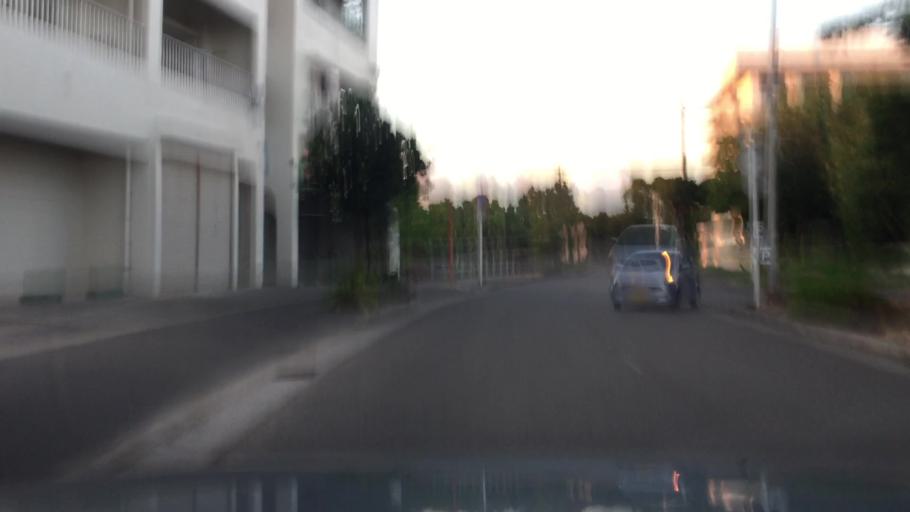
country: JP
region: Okinawa
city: Ishigaki
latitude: 24.3498
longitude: 124.1643
